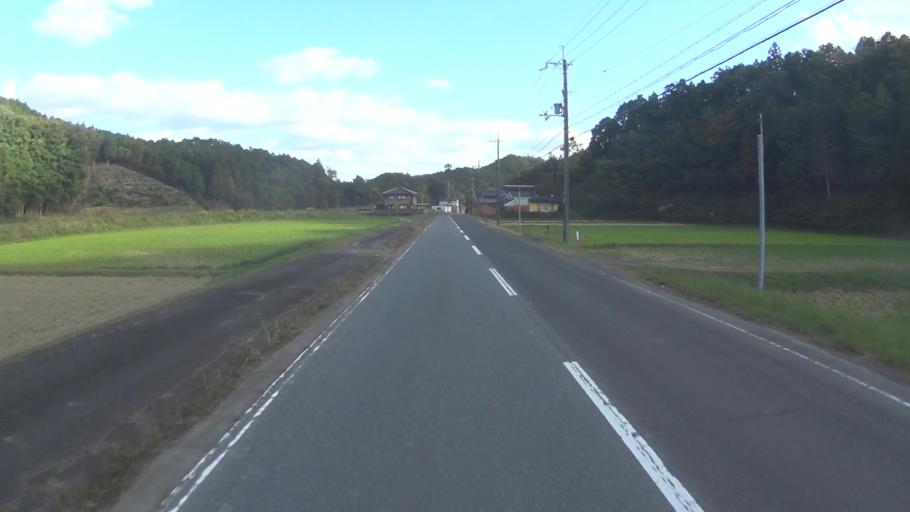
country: JP
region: Kyoto
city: Miyazu
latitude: 35.4413
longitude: 135.2156
